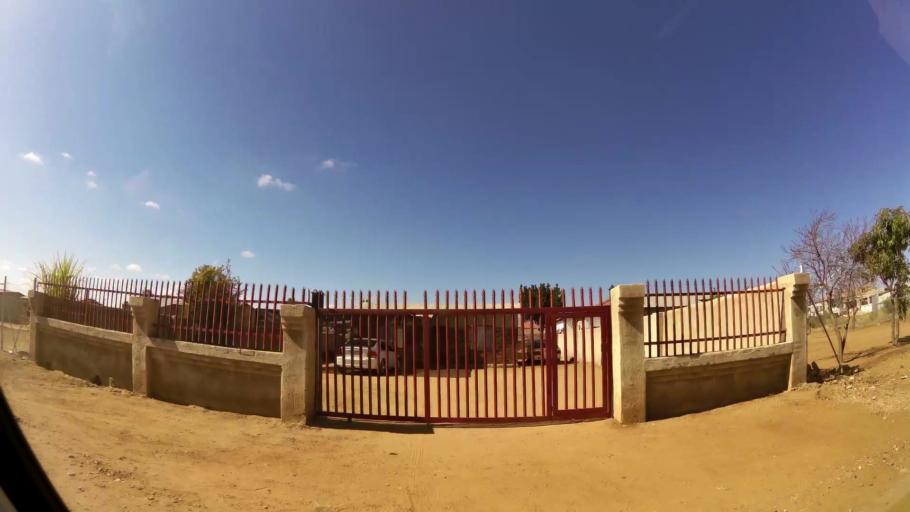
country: ZA
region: Limpopo
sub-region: Capricorn District Municipality
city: Polokwane
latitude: -23.8772
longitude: 29.4100
